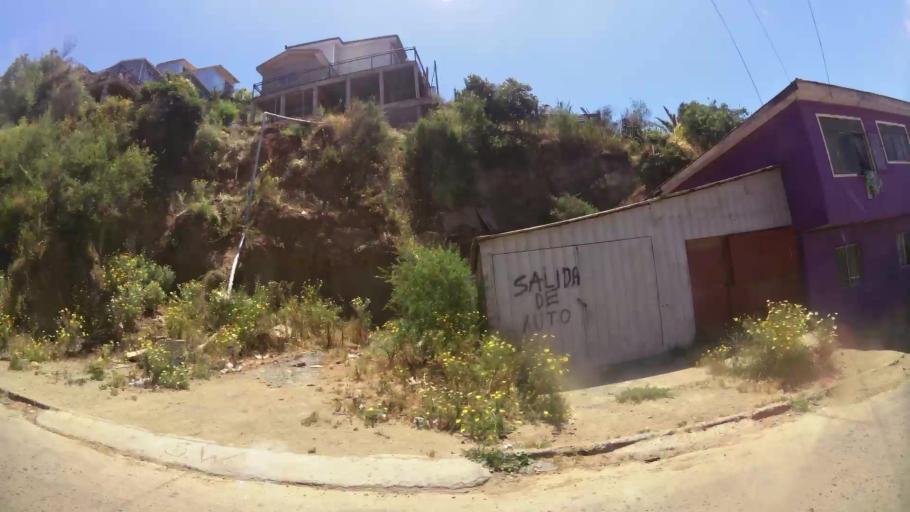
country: CL
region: Valparaiso
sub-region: Provincia de Valparaiso
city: Valparaiso
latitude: -33.0546
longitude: -71.6321
